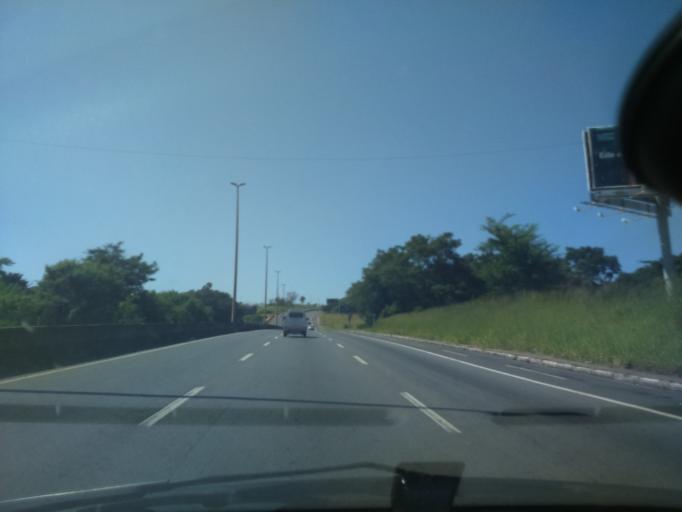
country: BR
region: Federal District
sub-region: Brasilia
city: Brasilia
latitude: -15.8419
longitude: -47.8223
